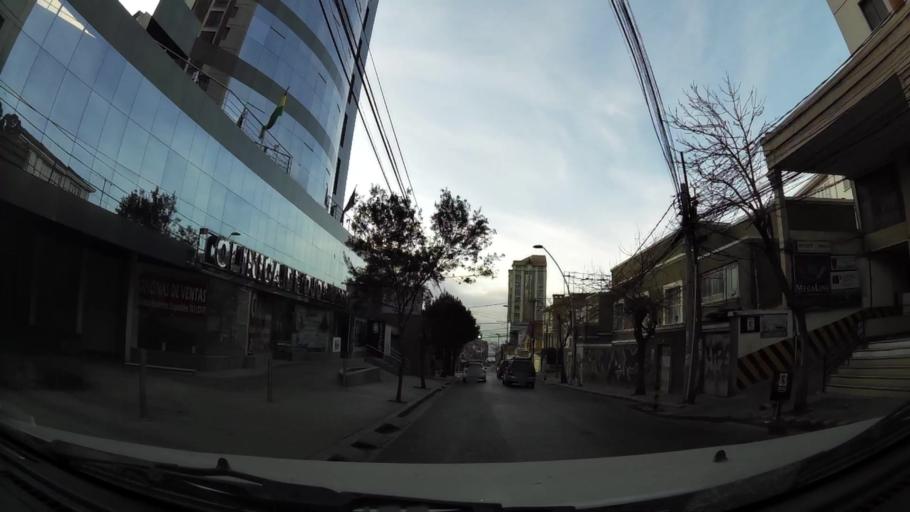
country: BO
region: La Paz
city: La Paz
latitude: -16.5117
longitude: -68.1264
